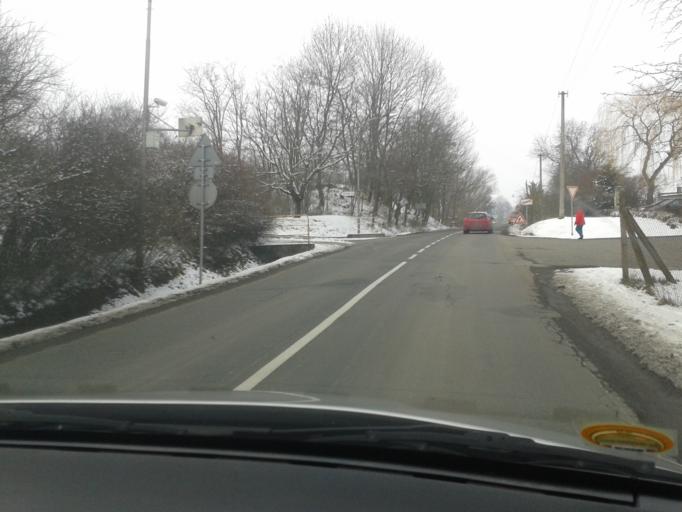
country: CZ
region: Olomoucky
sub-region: Okres Prostejov
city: Plumlov
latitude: 49.4884
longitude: 17.0171
